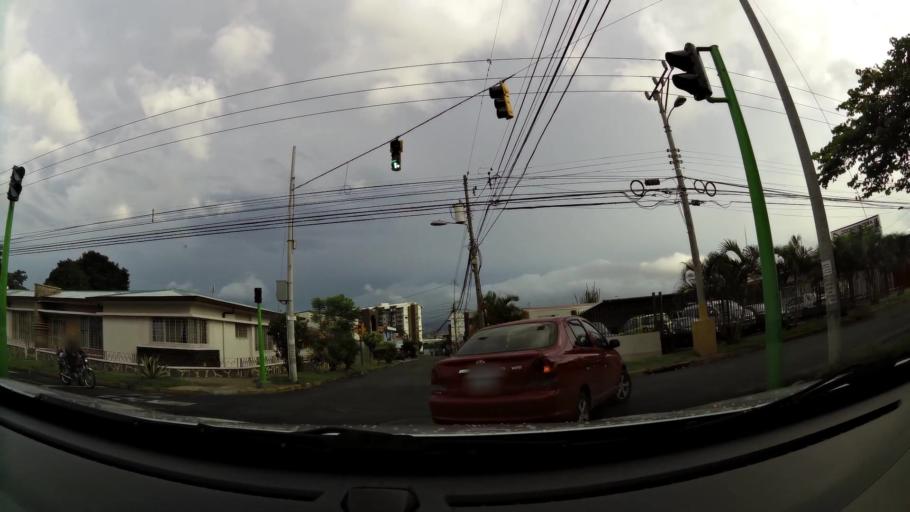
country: CR
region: San Jose
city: San Jose
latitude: 9.9385
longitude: -84.0952
